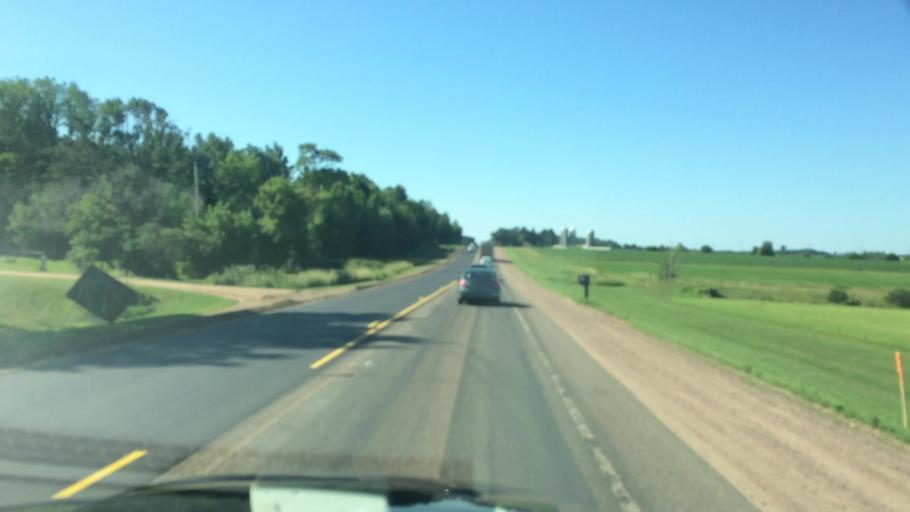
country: US
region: Wisconsin
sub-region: Marathon County
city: Stratford
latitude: 44.8697
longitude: -90.0791
